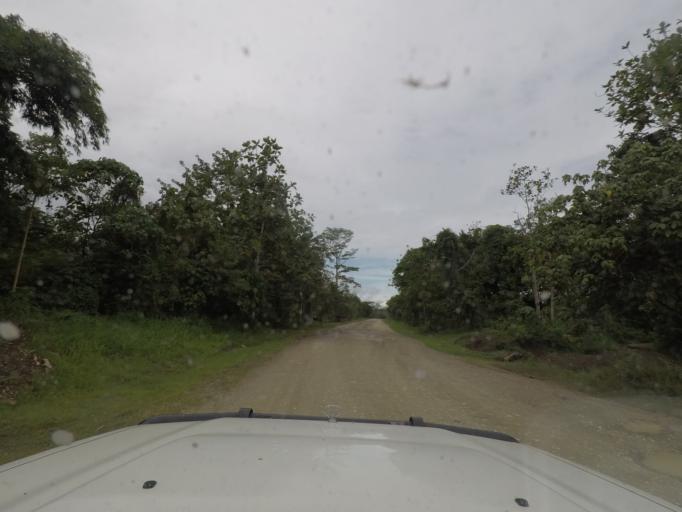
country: PG
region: Eastern Highlands
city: Goroka
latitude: -5.6517
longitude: 145.4941
